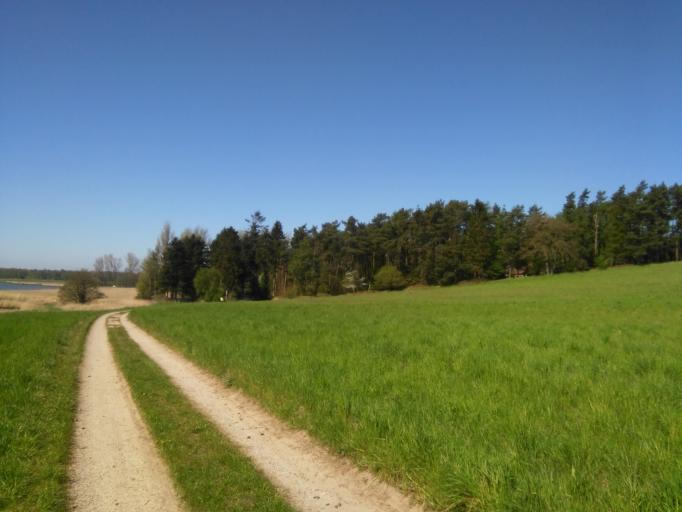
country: DK
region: Central Jutland
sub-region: Odder Kommune
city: Odder
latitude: 55.8852
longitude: 10.0801
